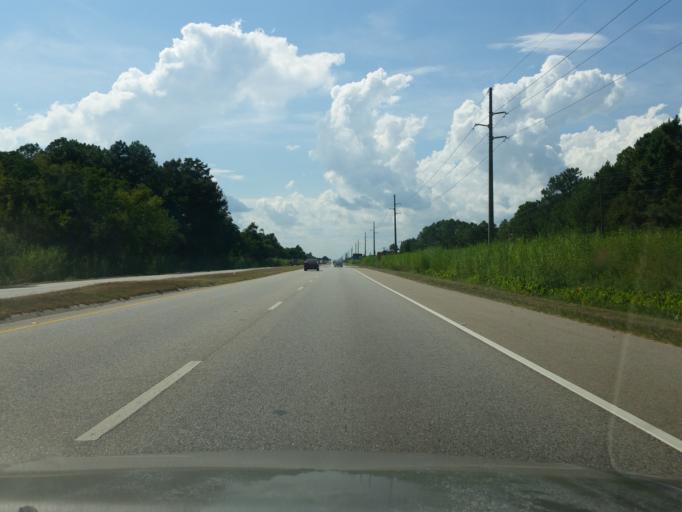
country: US
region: Alabama
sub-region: Baldwin County
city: Spanish Fort
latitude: 30.6692
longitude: -87.9321
